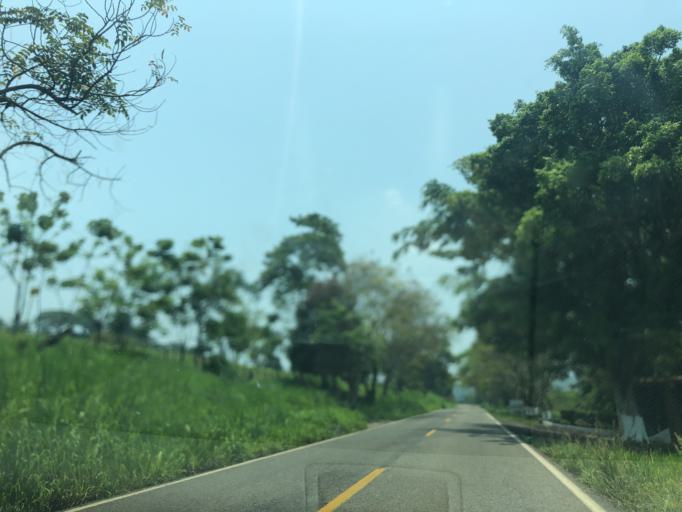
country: MX
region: Tabasco
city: Teapa
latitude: 17.5548
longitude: -92.9993
